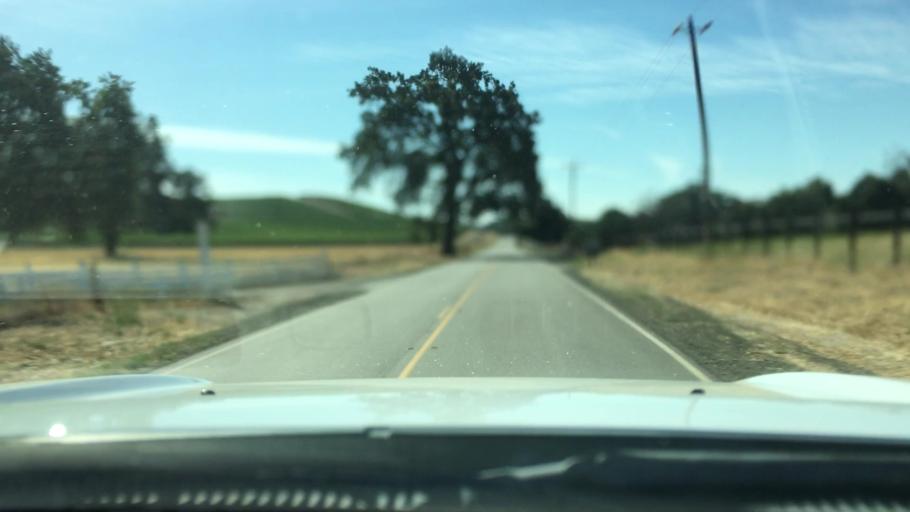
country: US
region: California
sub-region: San Luis Obispo County
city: Templeton
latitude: 35.5592
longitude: -120.6329
